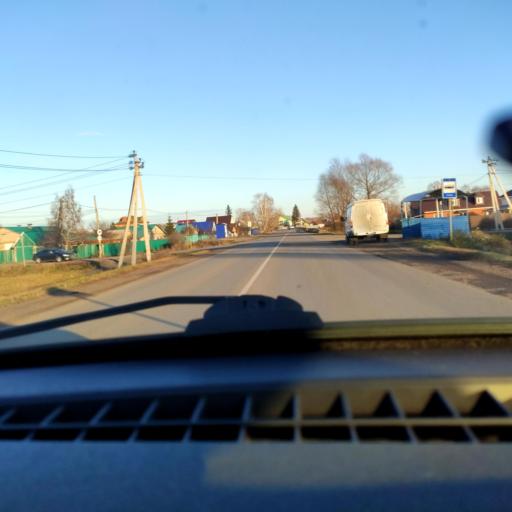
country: RU
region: Bashkortostan
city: Ufa
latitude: 54.6114
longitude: 55.8965
